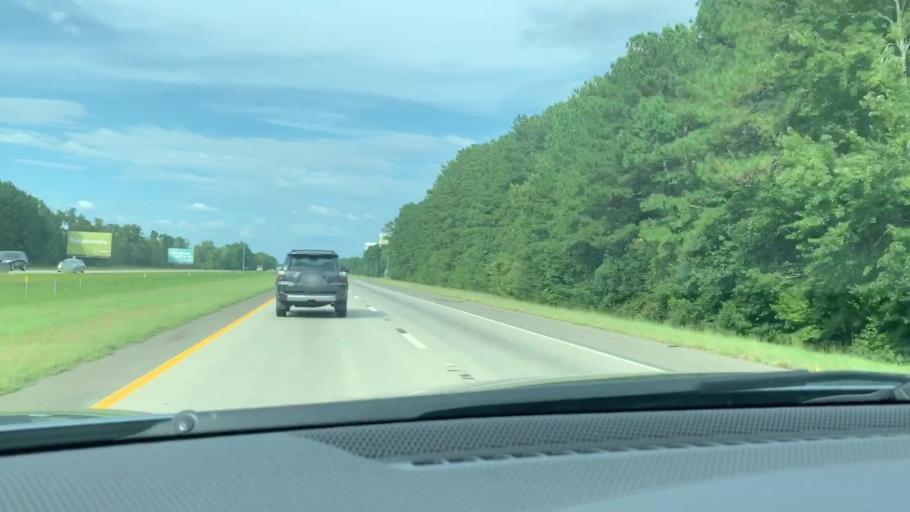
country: US
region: South Carolina
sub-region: Colleton County
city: Walterboro
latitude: 32.9524
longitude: -80.6816
